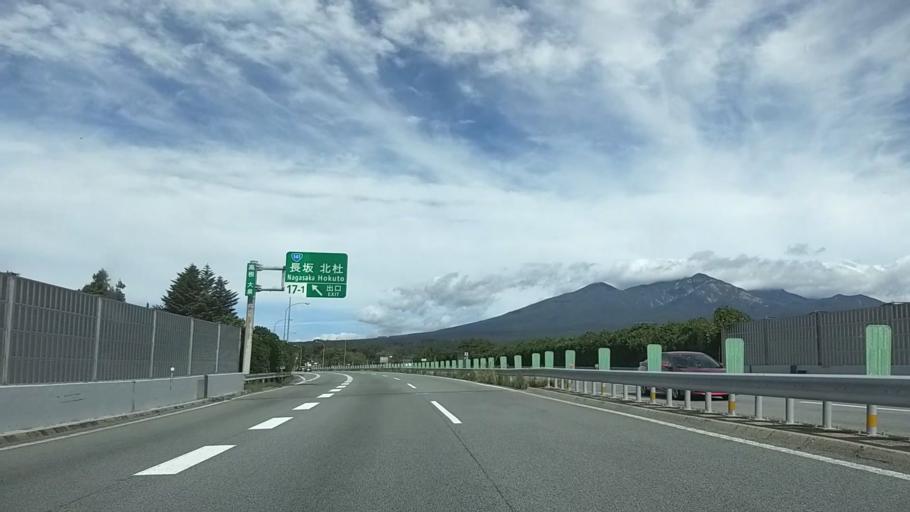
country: JP
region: Yamanashi
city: Nirasaki
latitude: 35.8337
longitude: 138.3914
